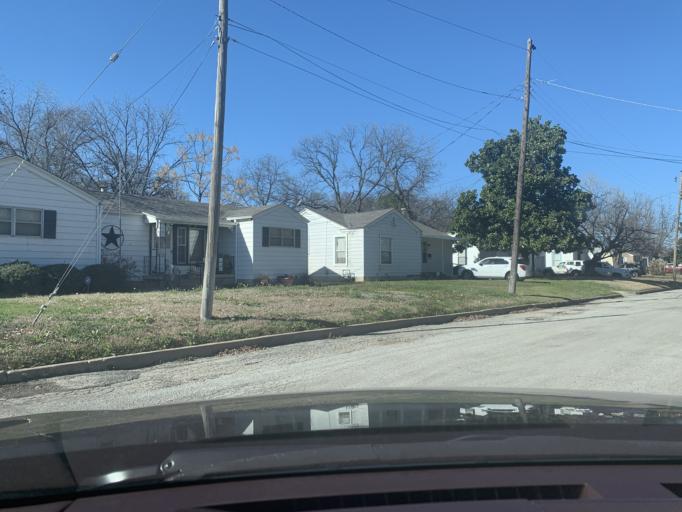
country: US
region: Texas
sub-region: Tarrant County
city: Haltom City
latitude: 32.7713
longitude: -97.2907
